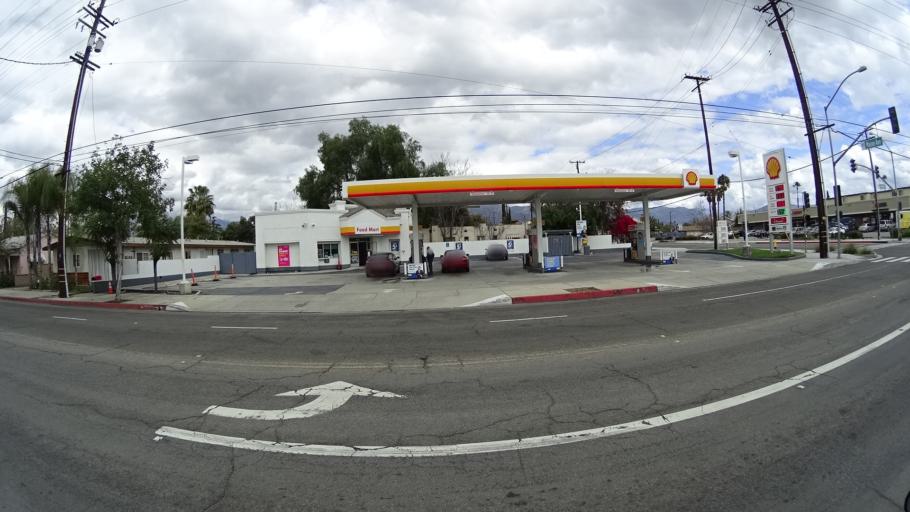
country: US
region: California
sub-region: Los Angeles County
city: Baldwin Park
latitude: 34.0922
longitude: -117.9609
